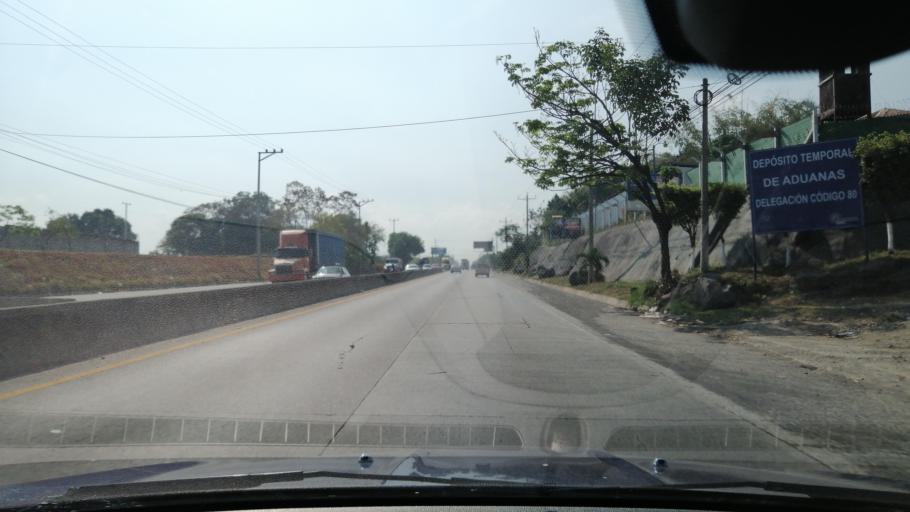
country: SV
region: La Libertad
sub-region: Distrito de Quezaltepeque
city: Quezaltepeque
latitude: 13.8040
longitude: -89.2363
